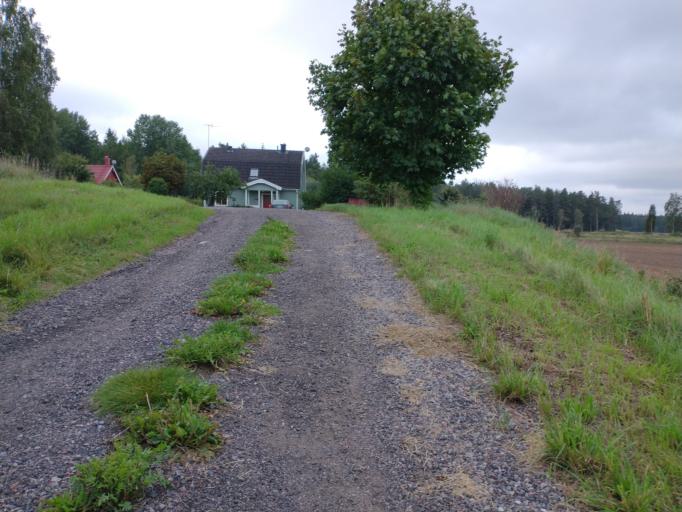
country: SE
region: Kalmar
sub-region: Kalmar Kommun
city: Lindsdal
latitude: 56.7794
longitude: 16.2967
